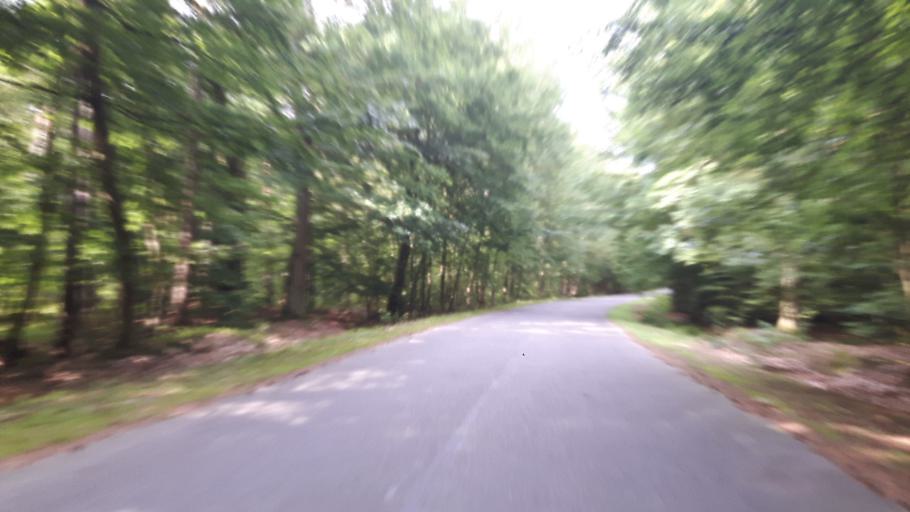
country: PL
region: West Pomeranian Voivodeship
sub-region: Powiat goleniowski
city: Nowogard
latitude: 53.7825
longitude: 15.1209
